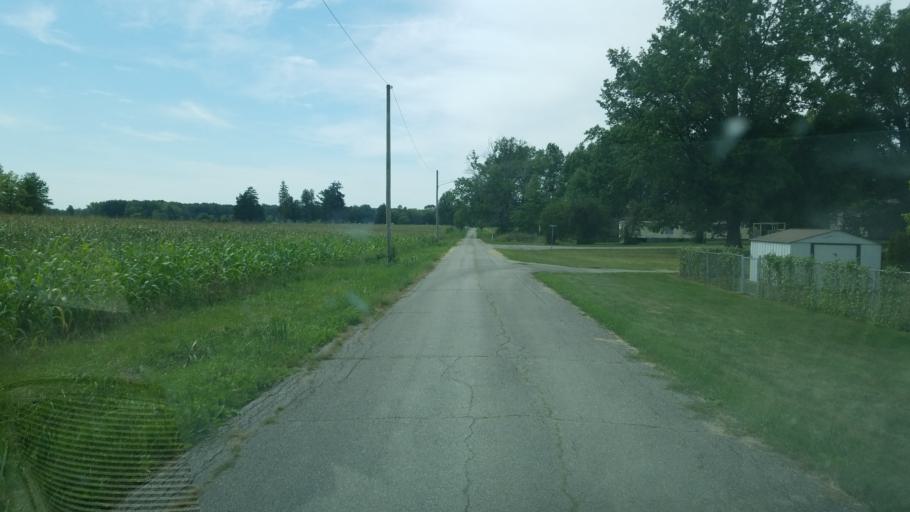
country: US
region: Ohio
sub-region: Union County
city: Richwood
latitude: 40.5821
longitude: -83.3174
